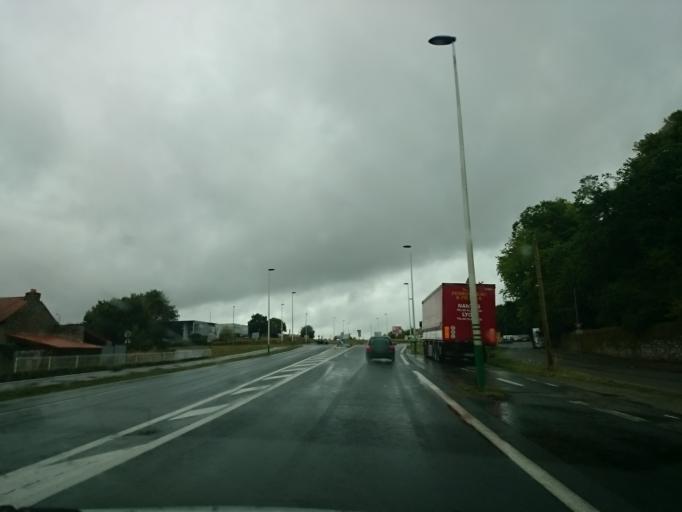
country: FR
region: Pays de la Loire
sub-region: Departement de la Loire-Atlantique
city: Saint-Herblain
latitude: 47.2259
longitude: -1.6521
